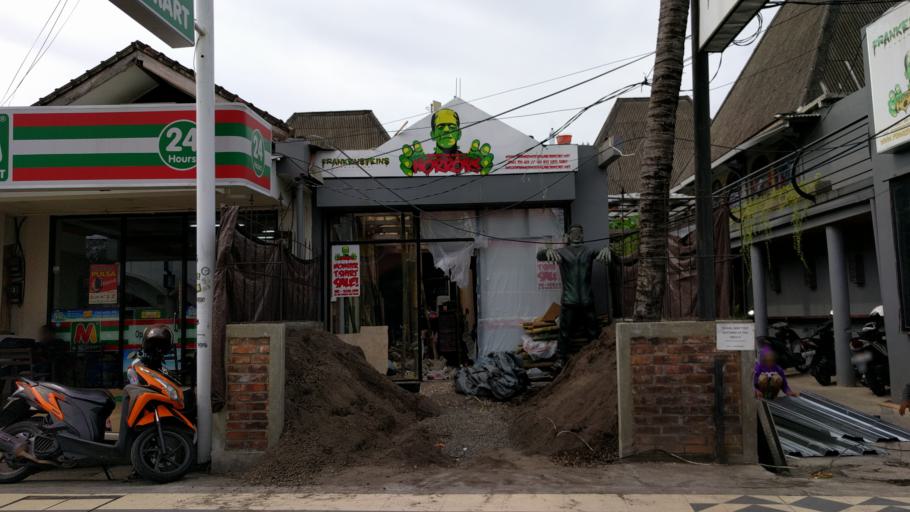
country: ID
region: Bali
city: Kuta
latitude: -8.6910
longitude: 115.1673
